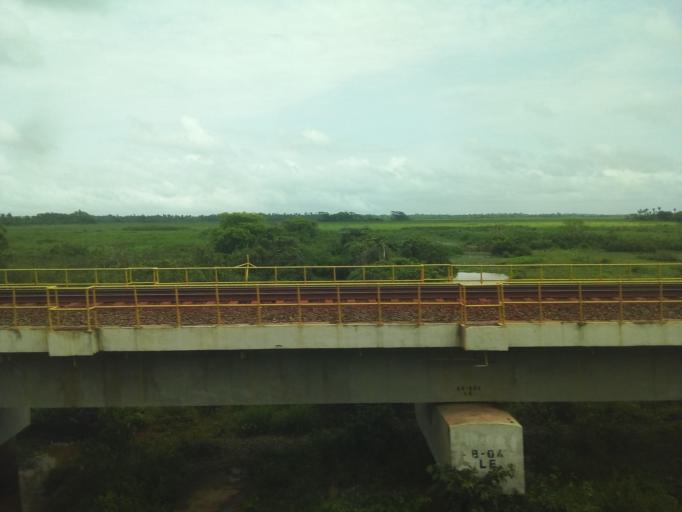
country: BR
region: Maranhao
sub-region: Arari
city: Arari
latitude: -3.5649
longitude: -44.6792
